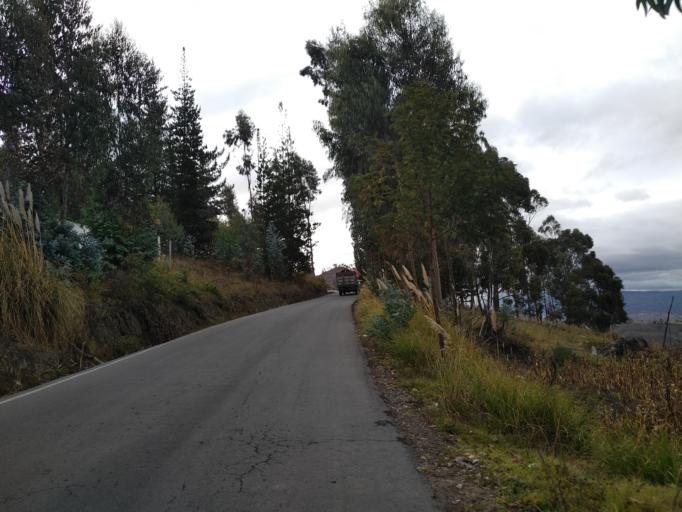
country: EC
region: Chimborazo
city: Riobamba
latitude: -1.7054
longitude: -78.6963
